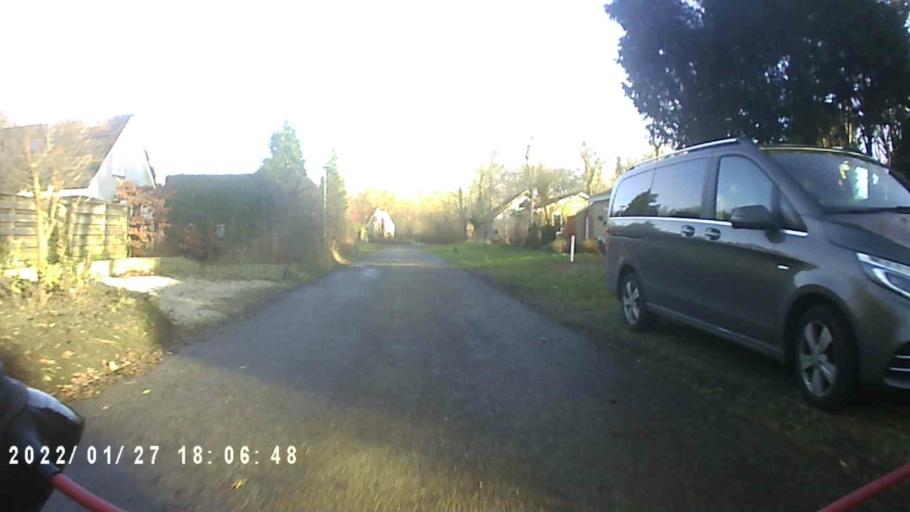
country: NL
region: Friesland
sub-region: Gemeente Dongeradeel
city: Anjum
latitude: 53.4053
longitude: 6.2197
